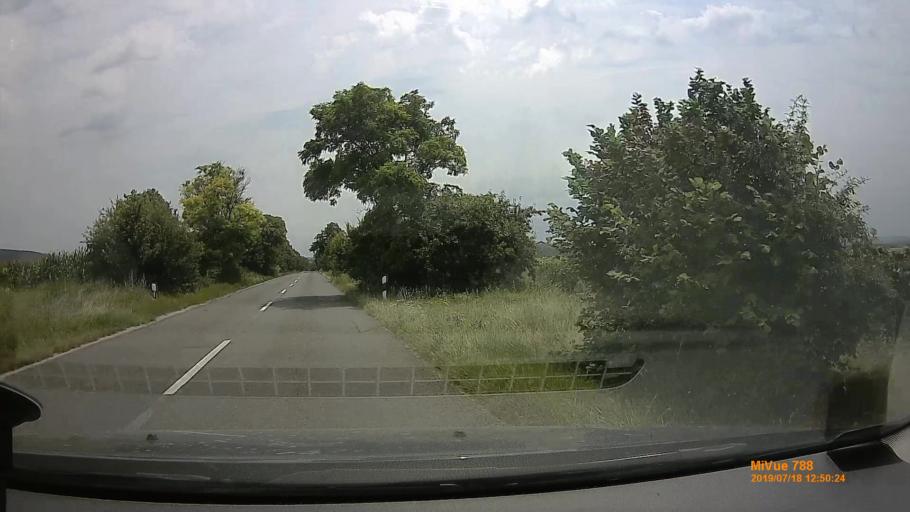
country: HU
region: Pest
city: Perbal
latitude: 47.5685
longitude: 18.7899
